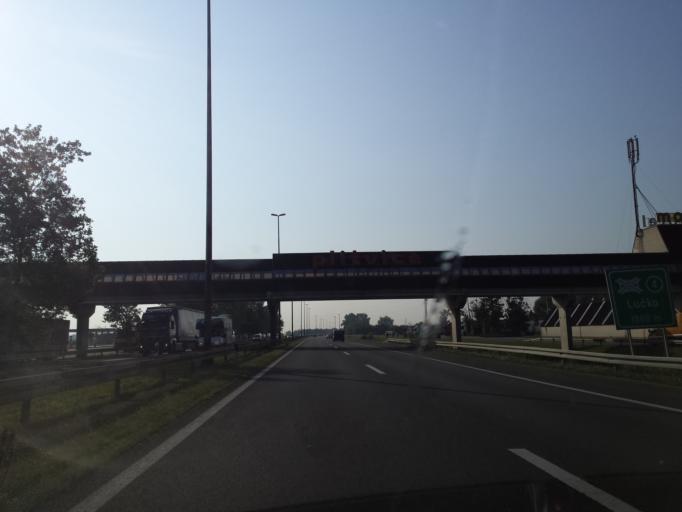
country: HR
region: Grad Zagreb
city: Lucko
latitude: 45.7747
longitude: 15.8791
